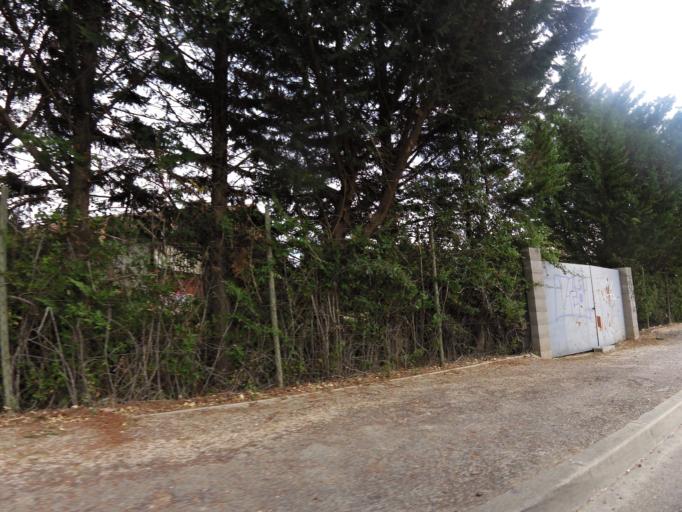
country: FR
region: Languedoc-Roussillon
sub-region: Departement du Gard
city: Saint-Genies-de-Malgoires
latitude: 43.9510
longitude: 4.2148
